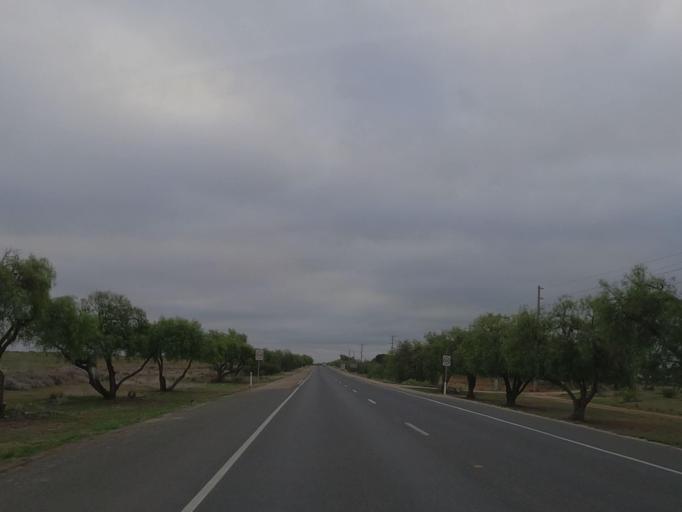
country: AU
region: Victoria
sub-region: Swan Hill
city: Swan Hill
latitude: -35.4495
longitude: 143.6233
